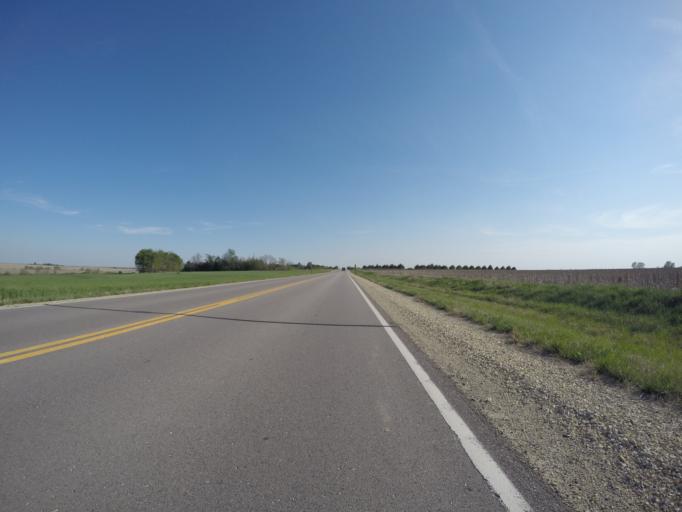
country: US
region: Kansas
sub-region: Riley County
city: Fort Riley North
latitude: 39.2930
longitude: -96.7750
